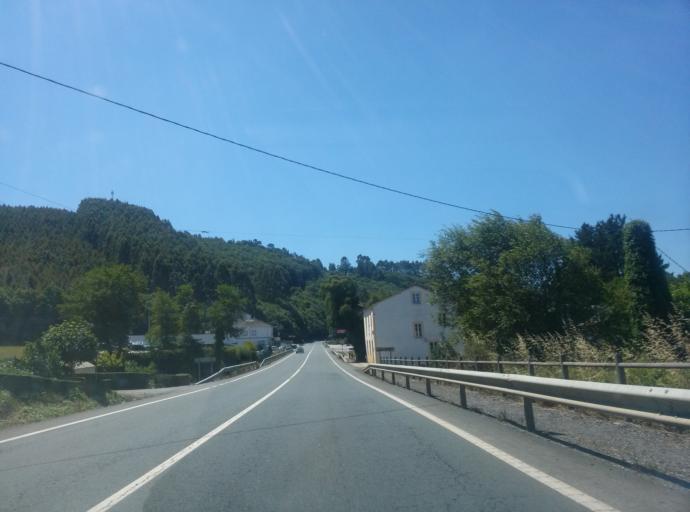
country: ES
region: Galicia
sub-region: Provincia de Lugo
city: Meira
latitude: 43.2155
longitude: -7.3059
